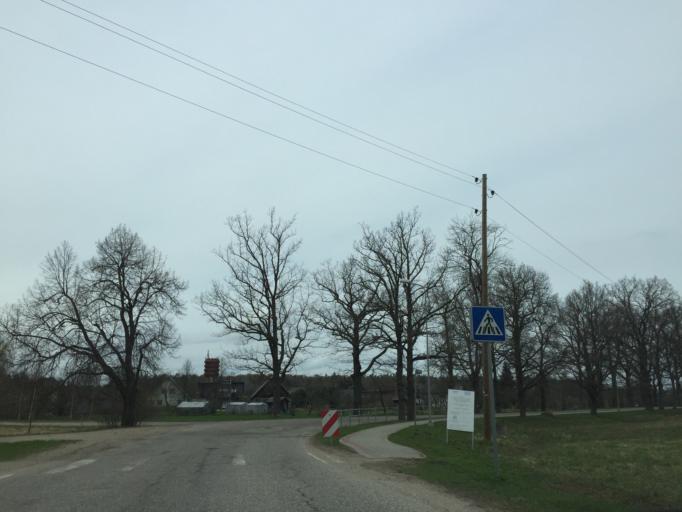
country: LV
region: Priekuli
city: Priekuli
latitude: 57.3481
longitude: 25.3314
